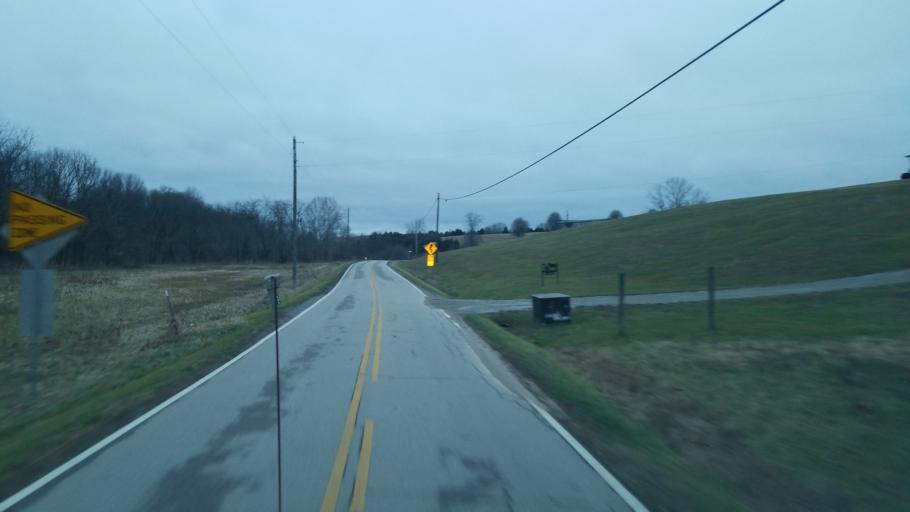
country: US
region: Kentucky
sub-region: Mason County
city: Maysville
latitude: 38.5383
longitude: -83.6941
